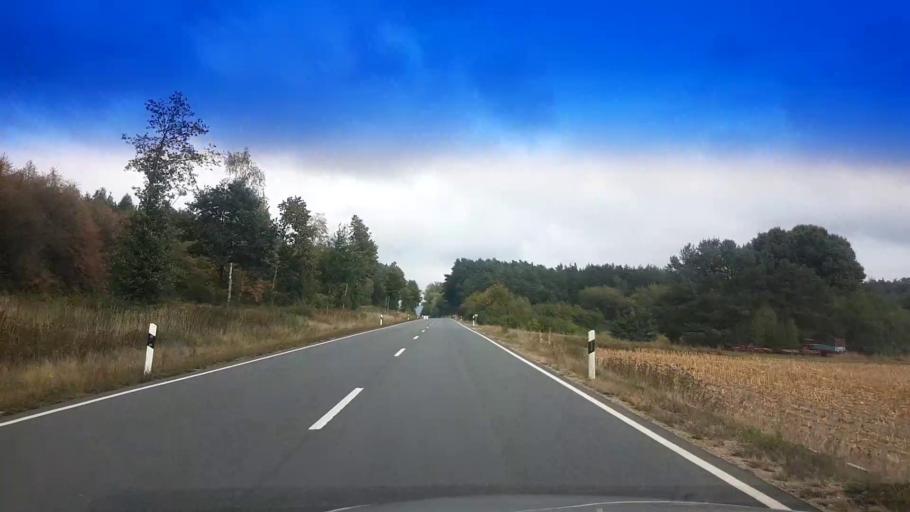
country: DE
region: Bavaria
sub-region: Upper Franconia
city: Hausen
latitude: 49.7023
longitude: 11.0249
